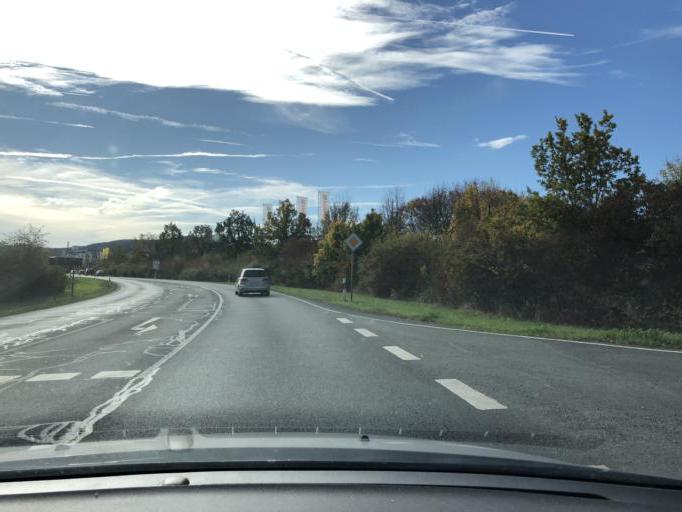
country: DE
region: Thuringia
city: Saalfeld
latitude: 50.6610
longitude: 11.3482
